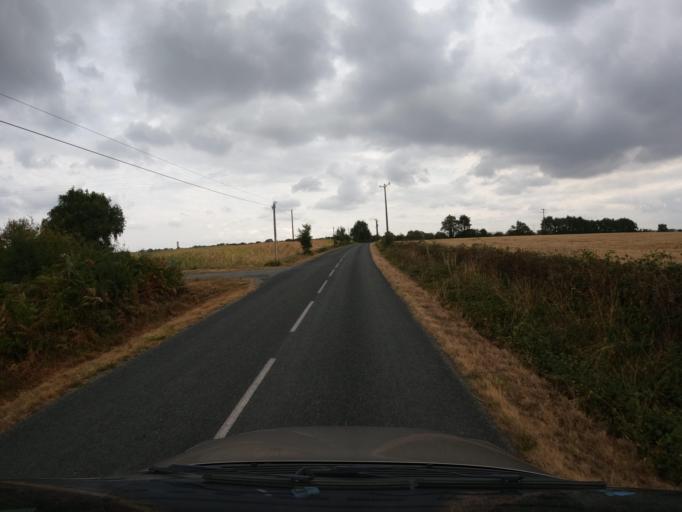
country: FR
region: Pays de la Loire
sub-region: Departement de Maine-et-Loire
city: Le Longeron
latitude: 47.0036
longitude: -1.0652
